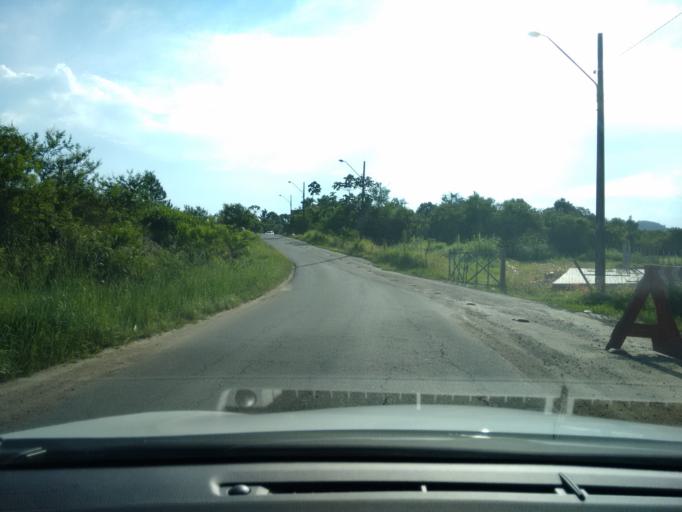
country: BR
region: Santa Catarina
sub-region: Blumenau
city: Blumenau
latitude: -26.8609
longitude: -49.0807
